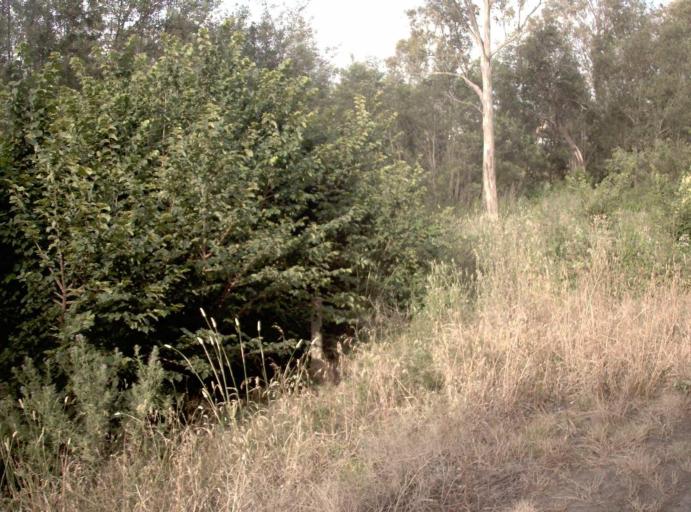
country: AU
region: Victoria
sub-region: Wellington
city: Sale
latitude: -37.9652
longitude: 146.9691
